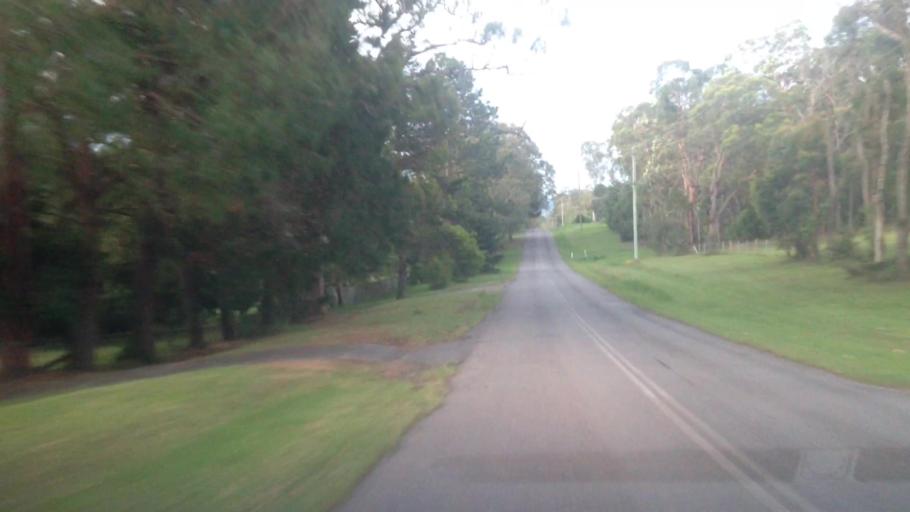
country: AU
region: New South Wales
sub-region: Lake Macquarie Shire
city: Cooranbong
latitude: -33.0813
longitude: 151.4725
